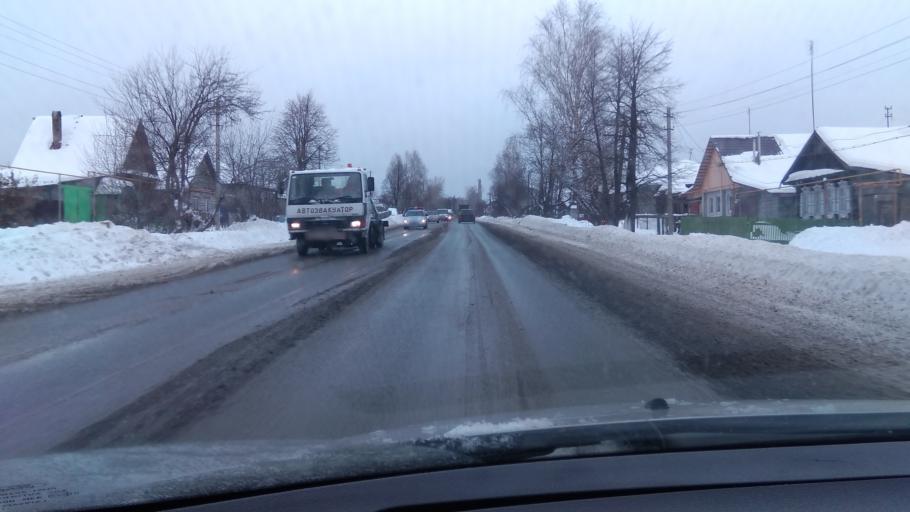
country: RU
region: Sverdlovsk
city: Nikolo-Pavlovskoye
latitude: 57.7897
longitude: 60.0556
